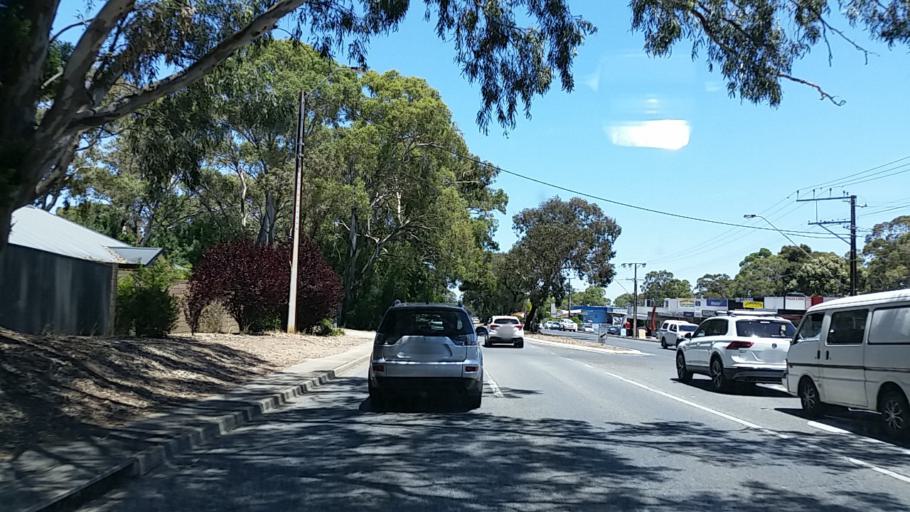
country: AU
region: South Australia
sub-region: Tea Tree Gully
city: Hope Valley
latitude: -34.8227
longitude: 138.7112
